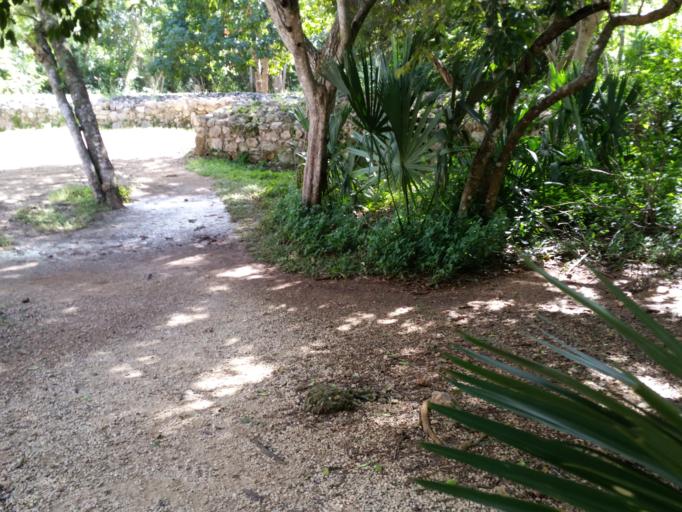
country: MX
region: Yucatan
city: Temozon
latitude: 20.8908
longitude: -88.1365
